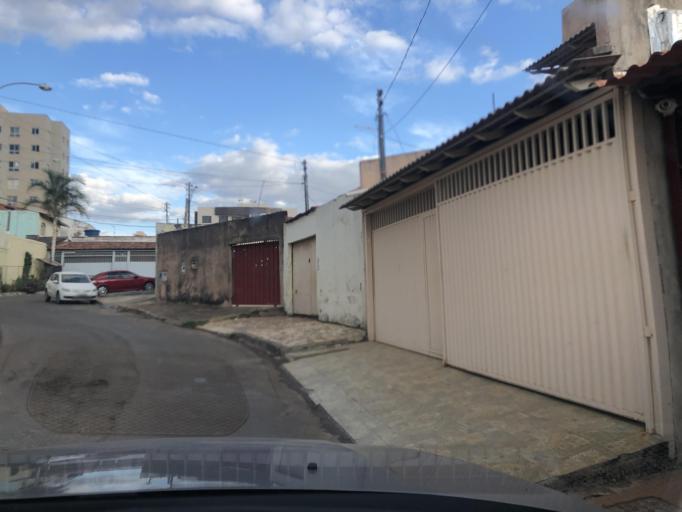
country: BR
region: Federal District
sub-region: Brasilia
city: Brasilia
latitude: -15.8706
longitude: -48.0951
